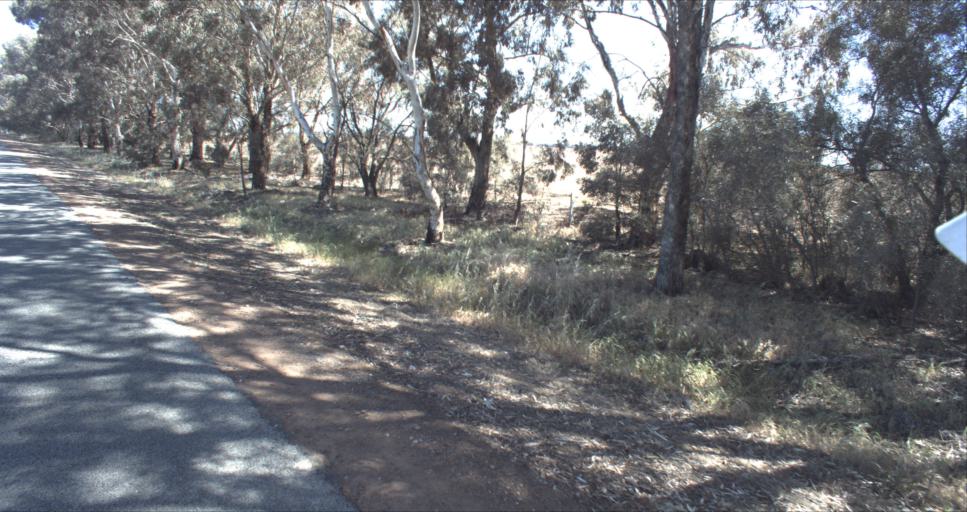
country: AU
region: New South Wales
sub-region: Leeton
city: Leeton
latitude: -34.5798
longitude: 146.2796
